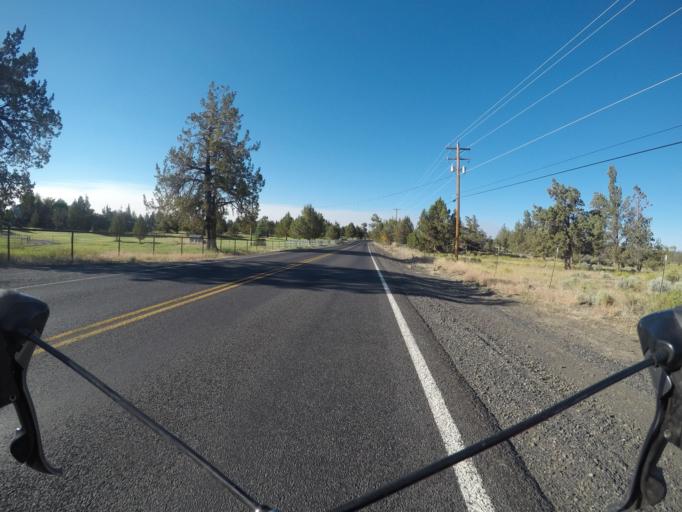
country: US
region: Oregon
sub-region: Deschutes County
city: Redmond
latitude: 44.1992
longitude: -121.2436
